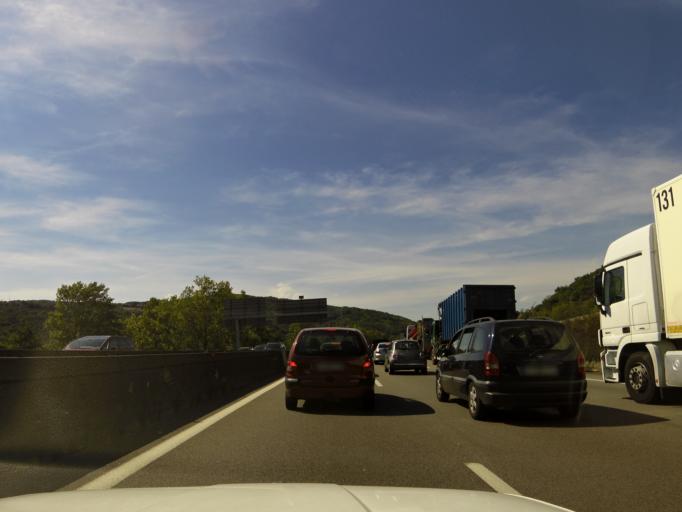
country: FR
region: Rhone-Alpes
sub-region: Departement de l'Isere
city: Seyssuel
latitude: 45.5436
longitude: 4.8446
